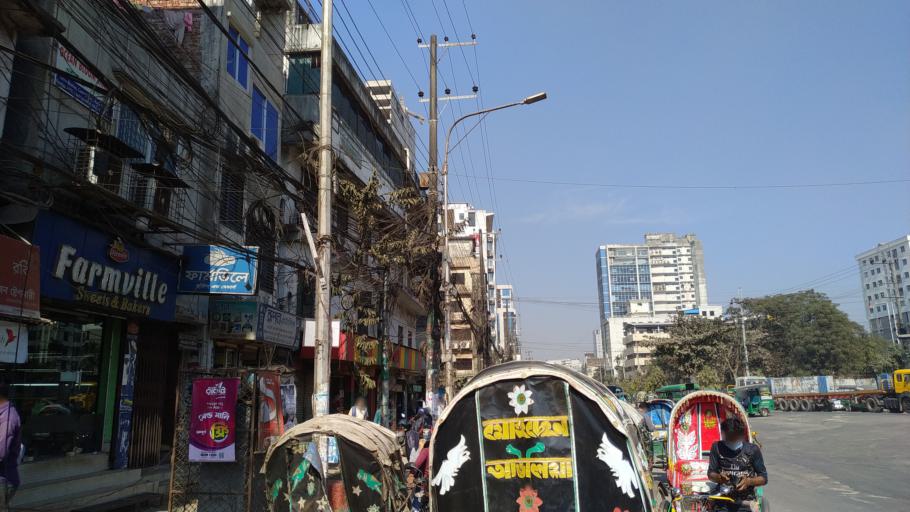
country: BD
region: Chittagong
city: Chittagong
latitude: 22.3194
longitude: 91.8119
